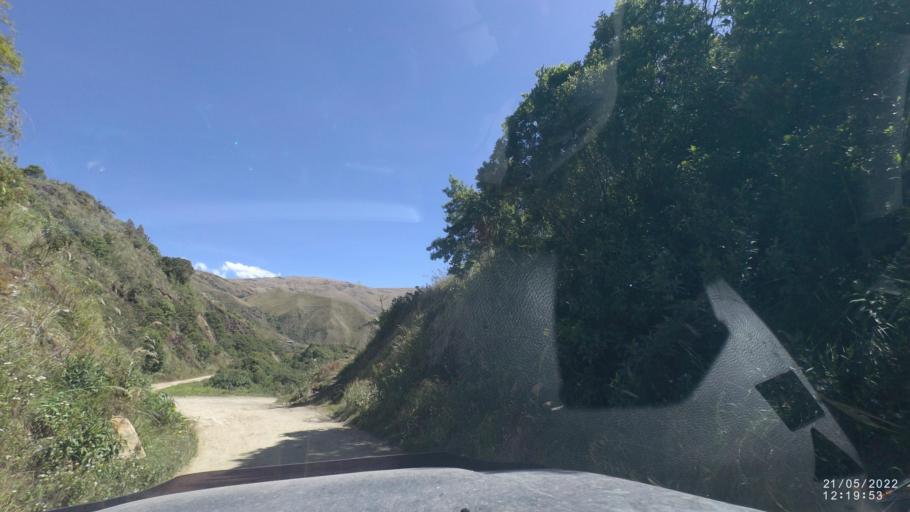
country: BO
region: Cochabamba
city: Colomi
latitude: -17.2255
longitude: -65.9030
